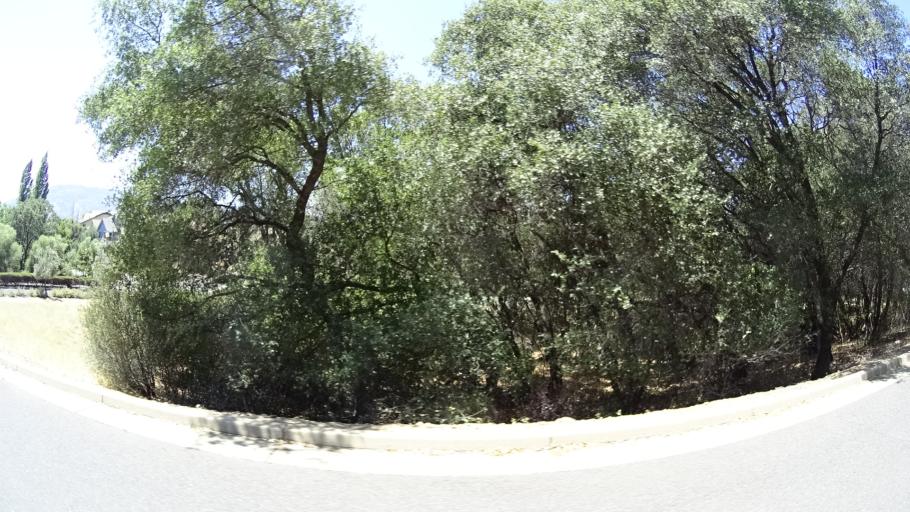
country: US
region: California
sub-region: Calaveras County
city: Angels Camp
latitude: 38.0683
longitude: -120.5512
